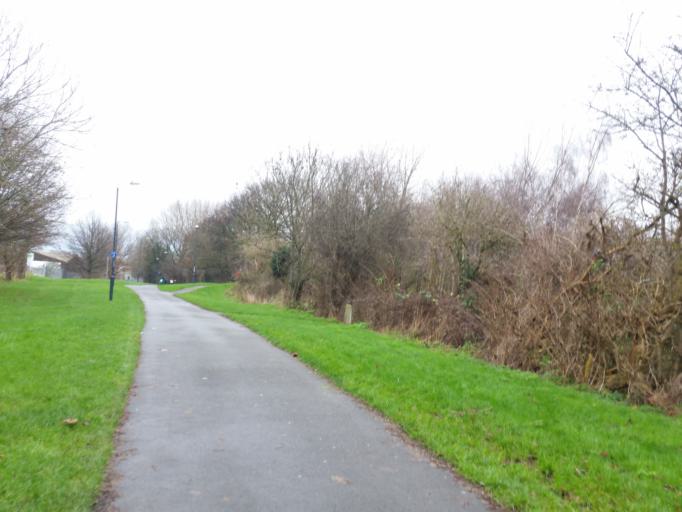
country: GB
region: England
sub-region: Derby
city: Derby
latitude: 52.8984
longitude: -1.4465
